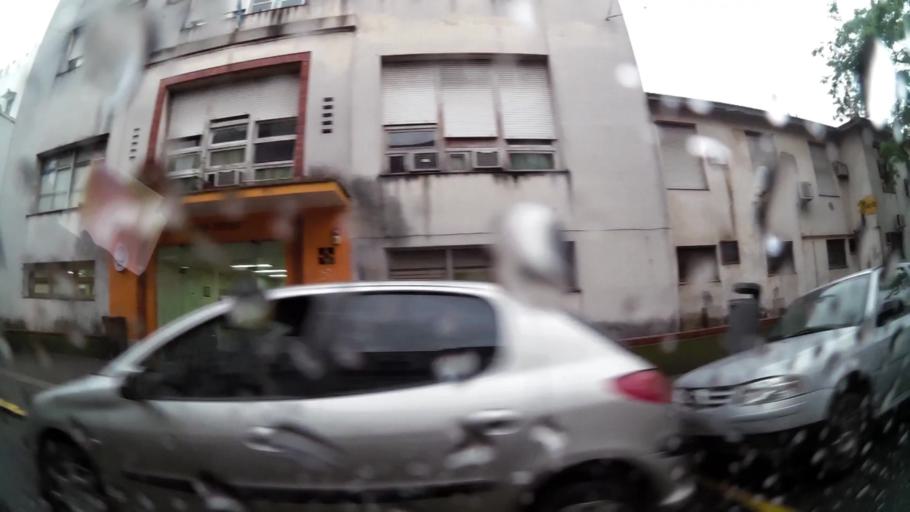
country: AR
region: Buenos Aires F.D.
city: Buenos Aires
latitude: -34.6303
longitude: -58.3757
